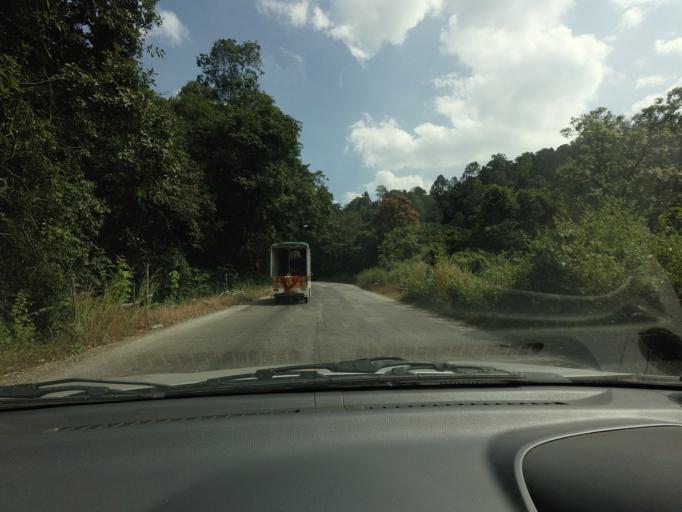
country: IN
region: Karnataka
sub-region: Hassan
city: Sakleshpur
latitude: 12.8292
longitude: 75.6313
